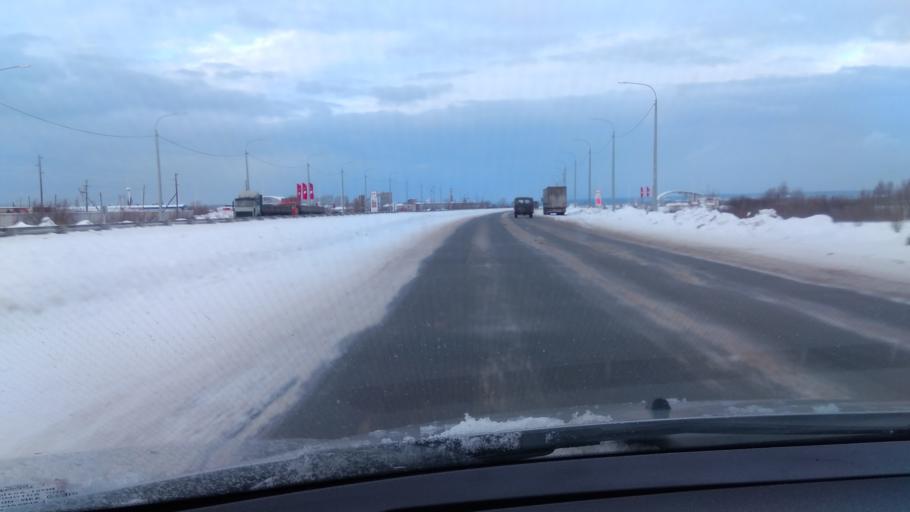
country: RU
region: Sverdlovsk
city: Tsementnyy
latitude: 57.4651
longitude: 60.1858
